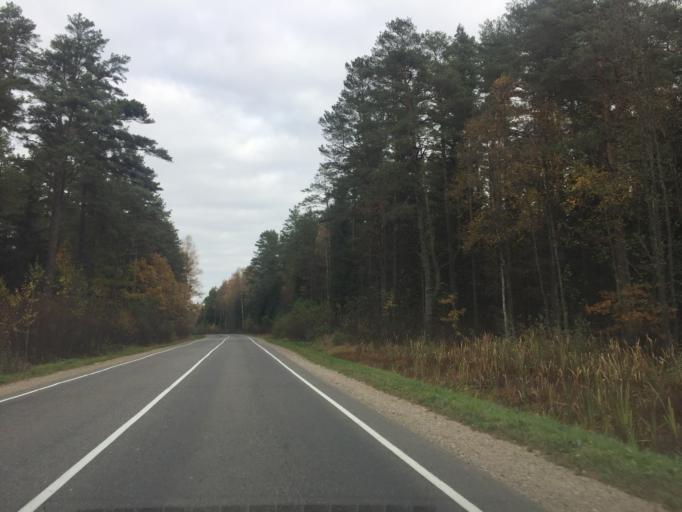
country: BY
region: Minsk
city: Svir
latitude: 54.8303
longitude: 26.1900
